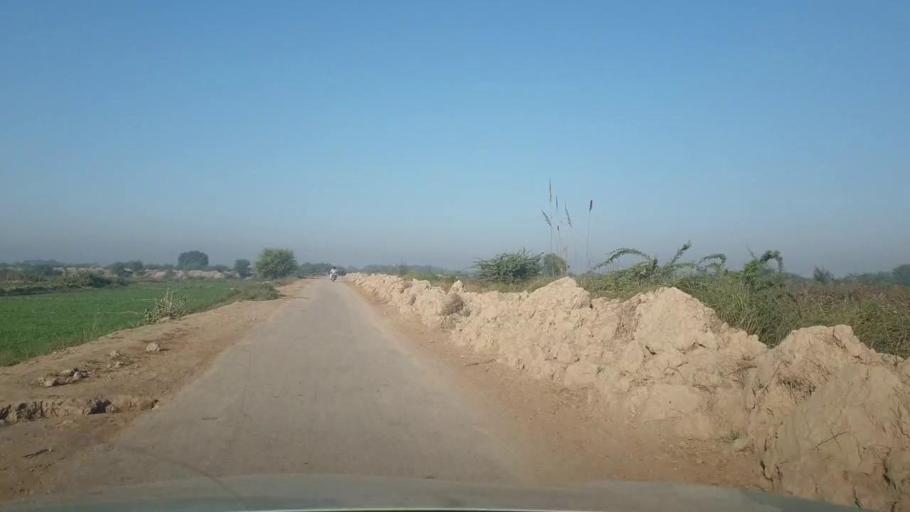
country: PK
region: Sindh
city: Bhan
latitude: 26.5495
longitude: 67.7047
